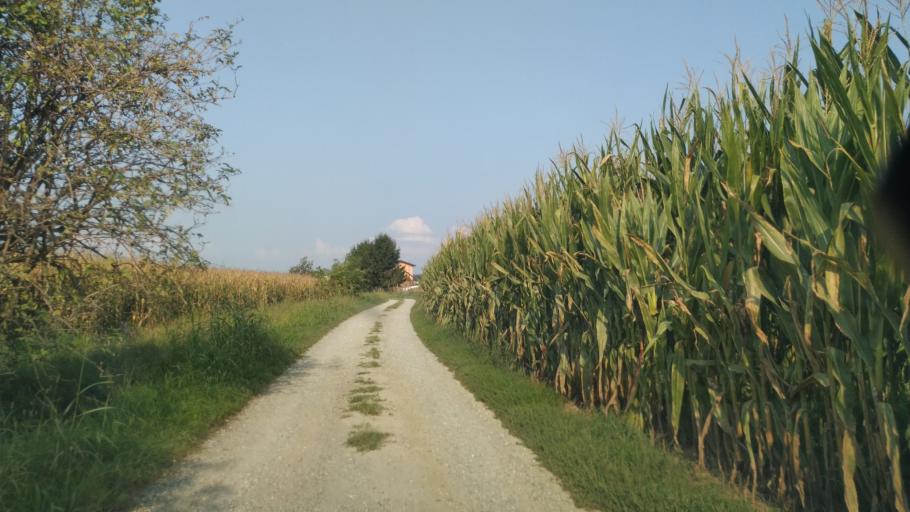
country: IT
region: Piedmont
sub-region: Provincia di Vercelli
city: Cigliano
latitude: 45.3254
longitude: 8.0307
